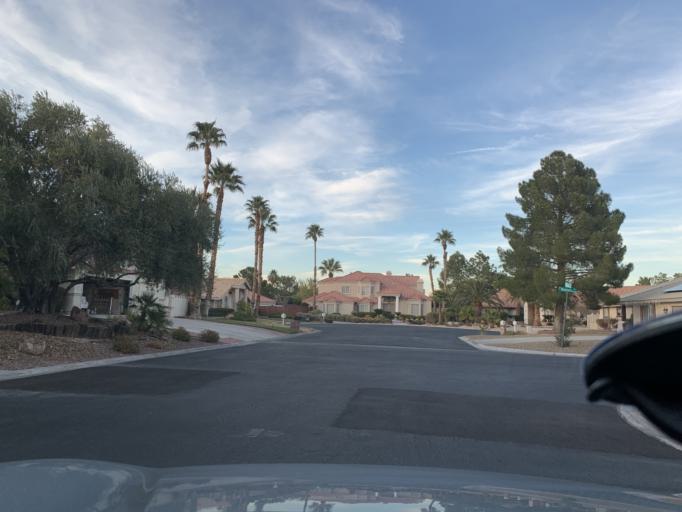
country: US
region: Nevada
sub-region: Clark County
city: Spring Valley
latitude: 36.0896
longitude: -115.2324
